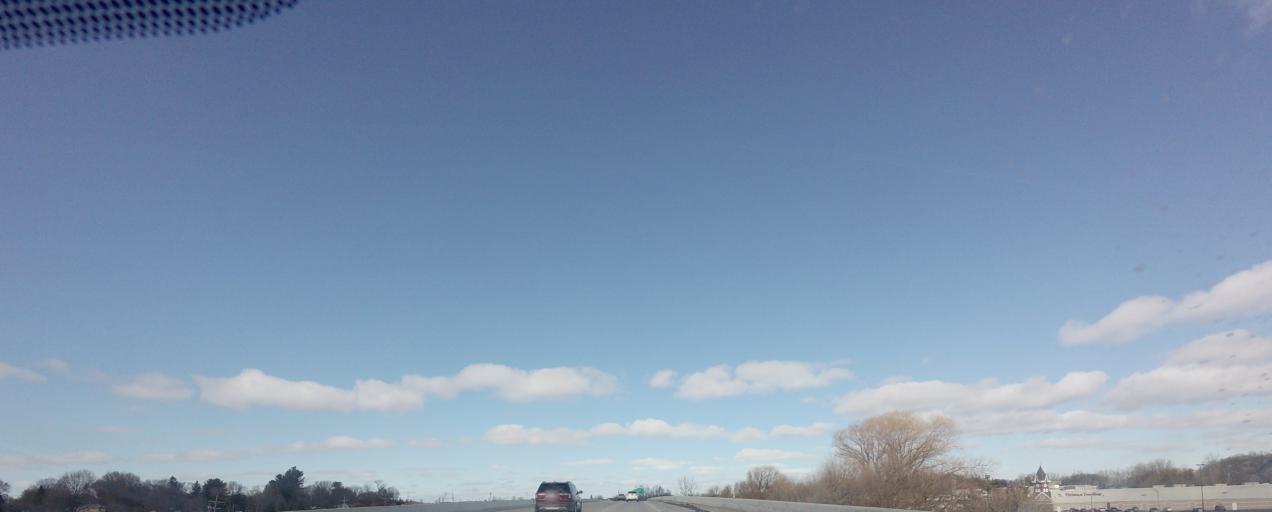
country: US
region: New York
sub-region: Onondaga County
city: Mattydale
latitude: 43.1095
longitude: -76.1479
